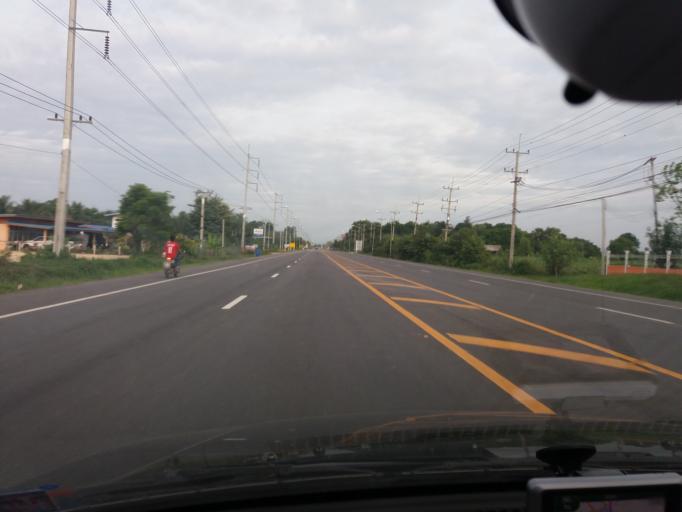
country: TH
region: Suphan Buri
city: U Thong
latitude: 14.3351
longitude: 99.7888
